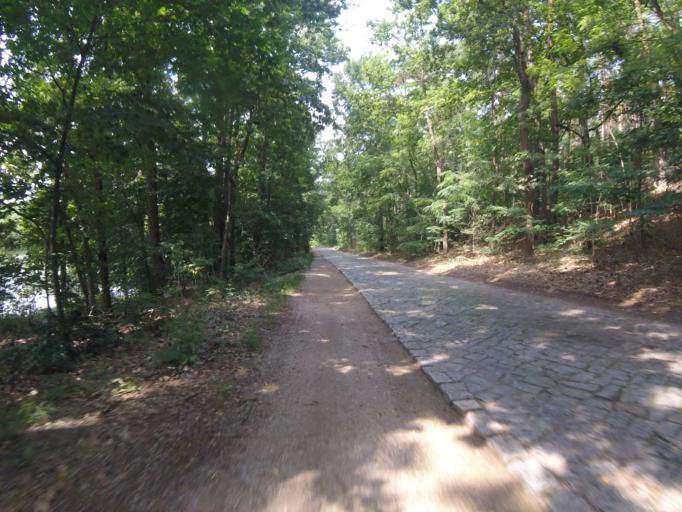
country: DE
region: Brandenburg
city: Schwerin
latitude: 52.1921
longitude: 13.5908
